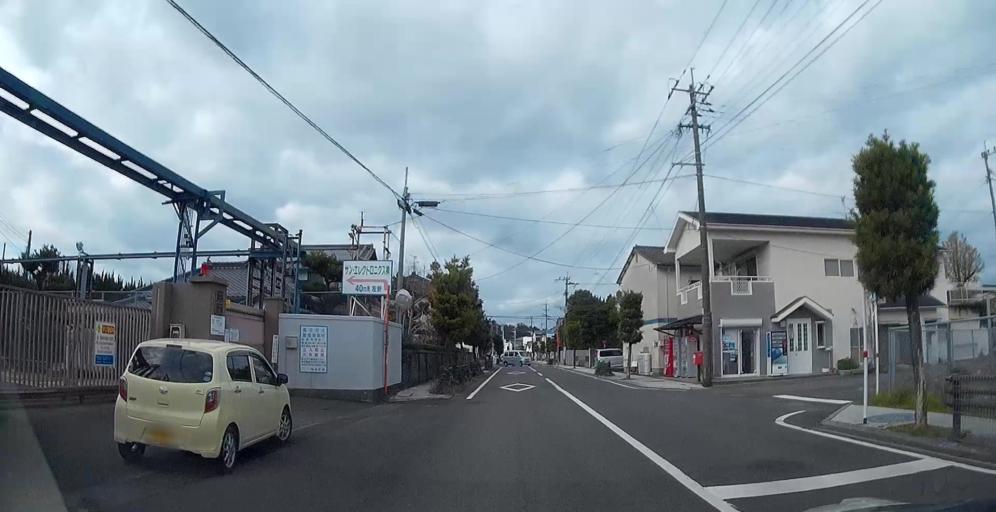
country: JP
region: Kumamoto
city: Minamata
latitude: 32.2114
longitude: 130.3918
